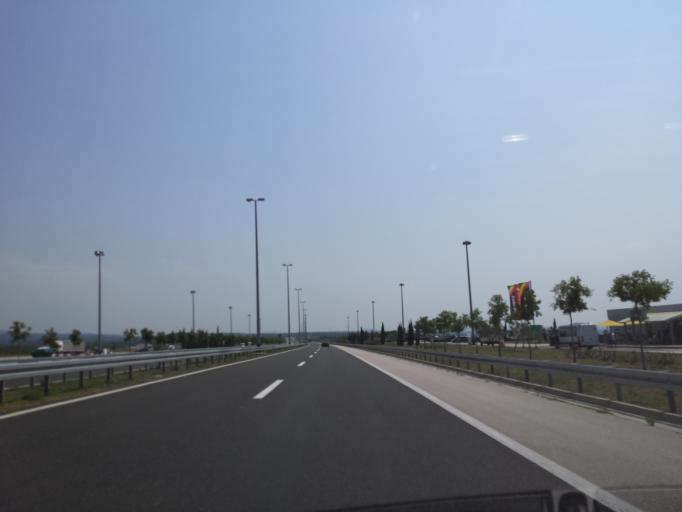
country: HR
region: Zadarska
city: Polaca
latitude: 44.0633
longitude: 15.5288
